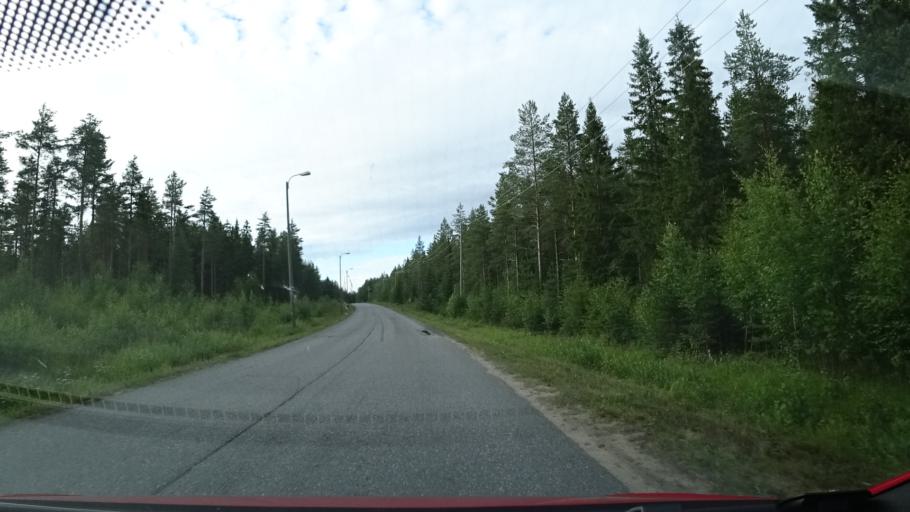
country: FI
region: Northern Ostrobothnia
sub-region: Oulu
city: Haukipudas
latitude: 65.1978
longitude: 25.4136
